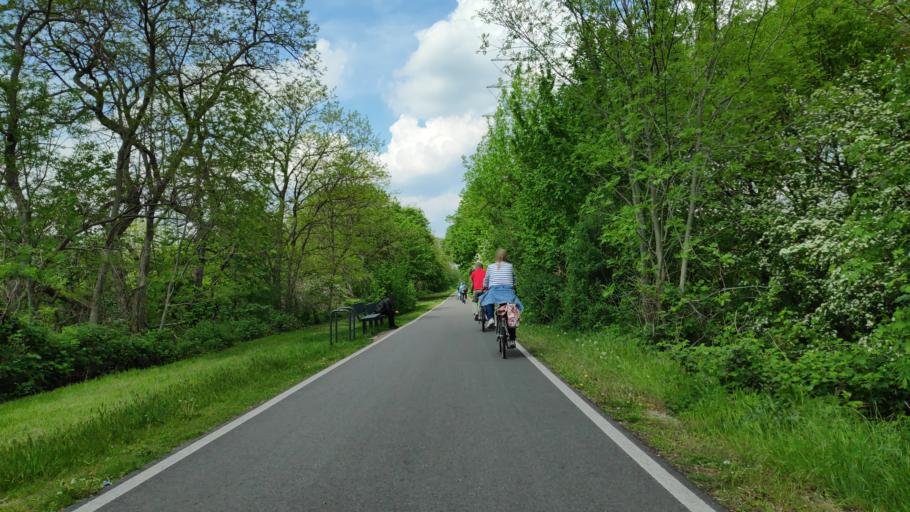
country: DE
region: North Rhine-Westphalia
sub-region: Regierungsbezirk Munster
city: Gelsenkirchen
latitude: 51.5312
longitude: 7.1339
